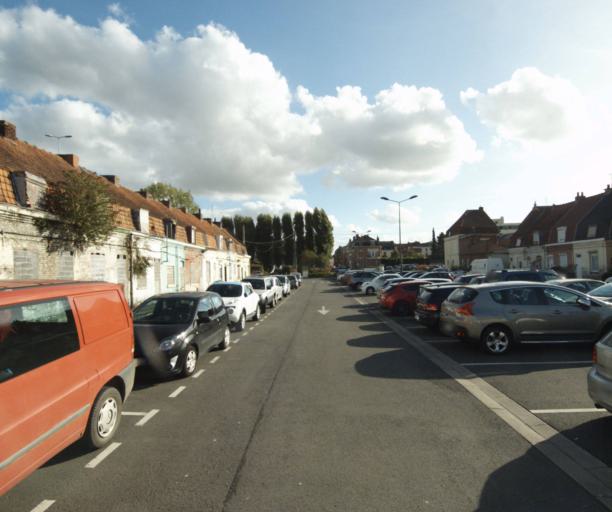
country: FR
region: Nord-Pas-de-Calais
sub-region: Departement du Nord
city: Armentieres
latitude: 50.6891
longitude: 2.8856
